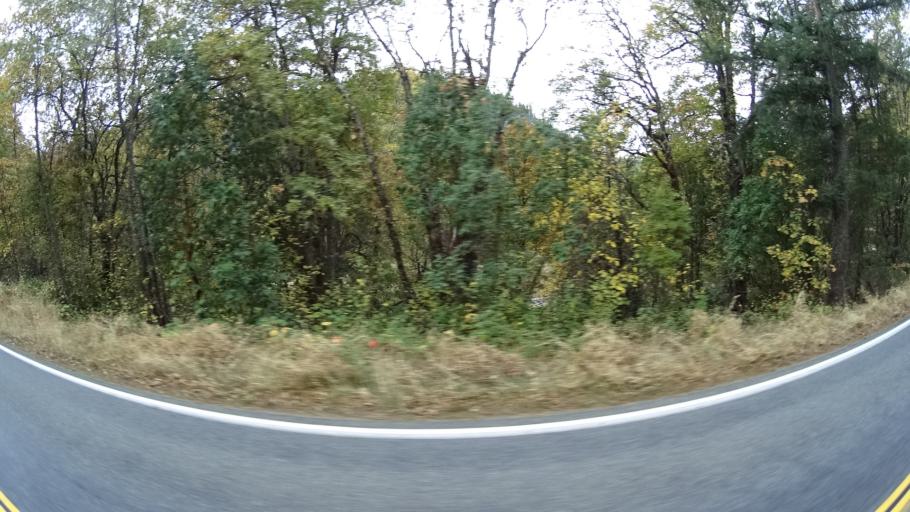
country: US
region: California
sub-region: Siskiyou County
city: Happy Camp
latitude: 41.8826
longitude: -123.4228
